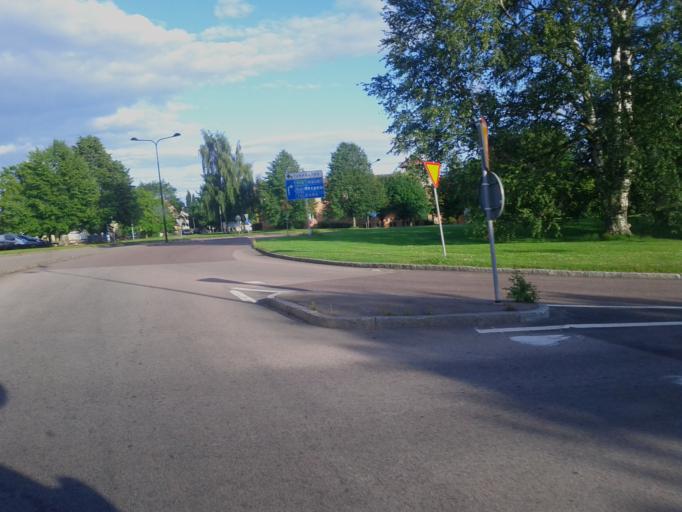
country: SE
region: Dalarna
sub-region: Borlange Kommun
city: Borlaenge
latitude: 60.4820
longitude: 15.4275
